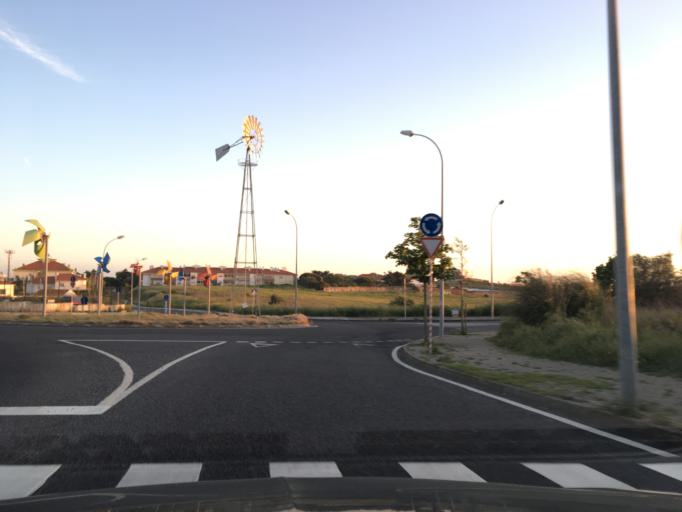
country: PT
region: Lisbon
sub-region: Oeiras
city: Terrugem
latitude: 38.7075
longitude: -9.2874
